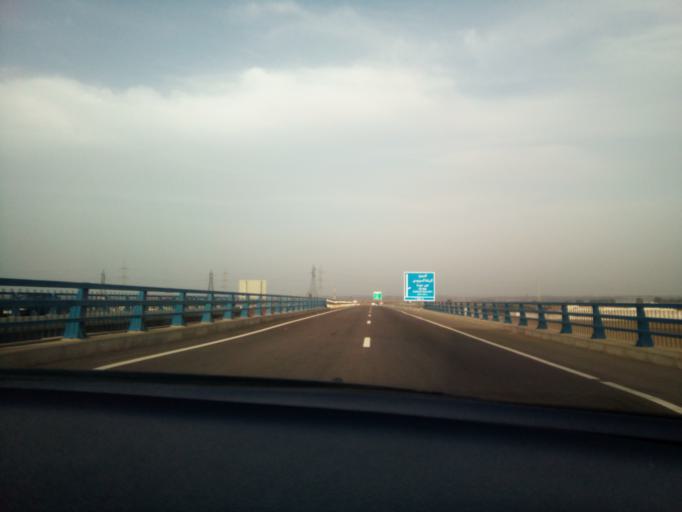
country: MA
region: Rabat-Sale-Zemmour-Zaer
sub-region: Skhirate-Temara
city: Temara
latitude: 33.8437
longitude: -6.8457
